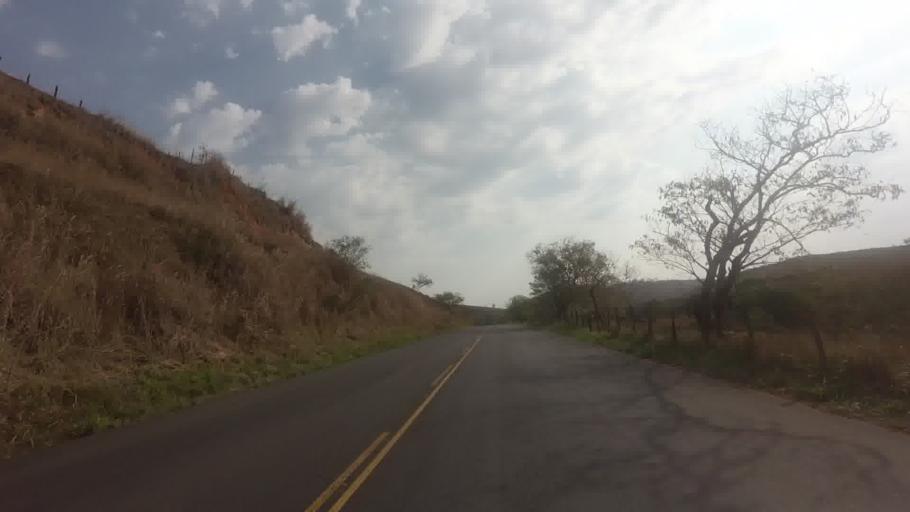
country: BR
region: Rio de Janeiro
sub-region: Itaperuna
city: Itaperuna
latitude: -21.3448
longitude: -41.9028
